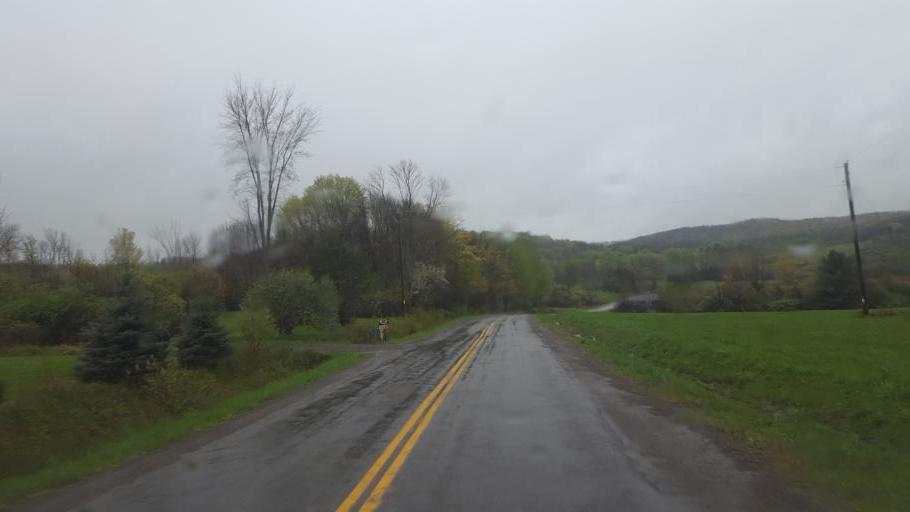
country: US
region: Pennsylvania
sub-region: Tioga County
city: Elkland
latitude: 42.0412
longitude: -77.4021
